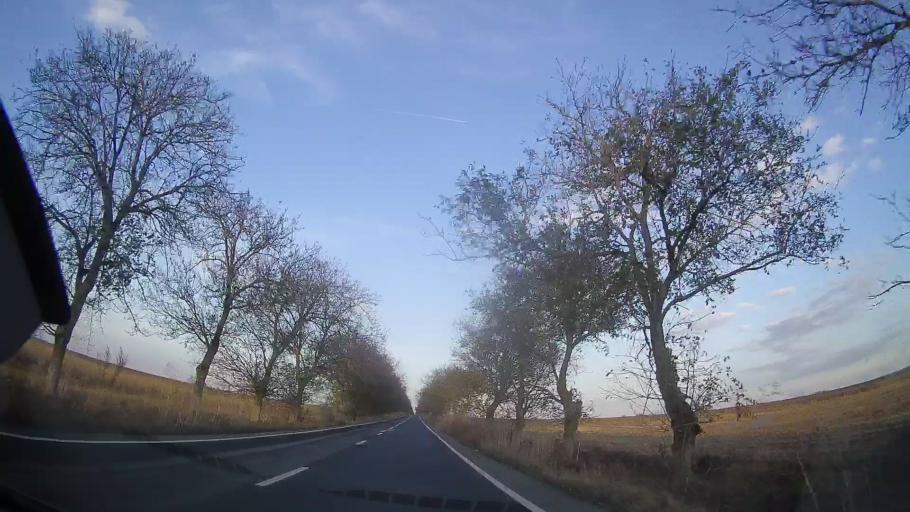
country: RO
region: Constanta
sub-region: Comuna Chirnogeni
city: Chirnogeni
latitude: 43.8523
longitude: 28.2446
